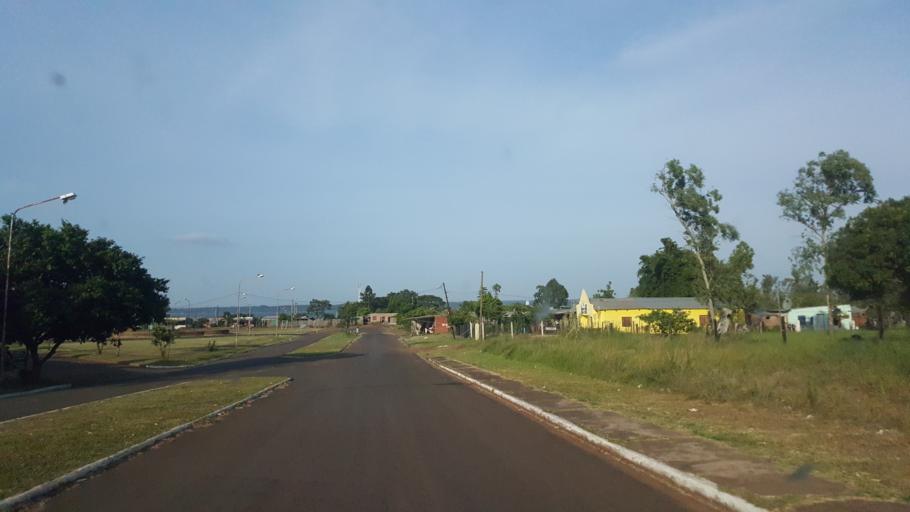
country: AR
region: Misiones
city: Garupa
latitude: -27.4357
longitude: -55.8680
